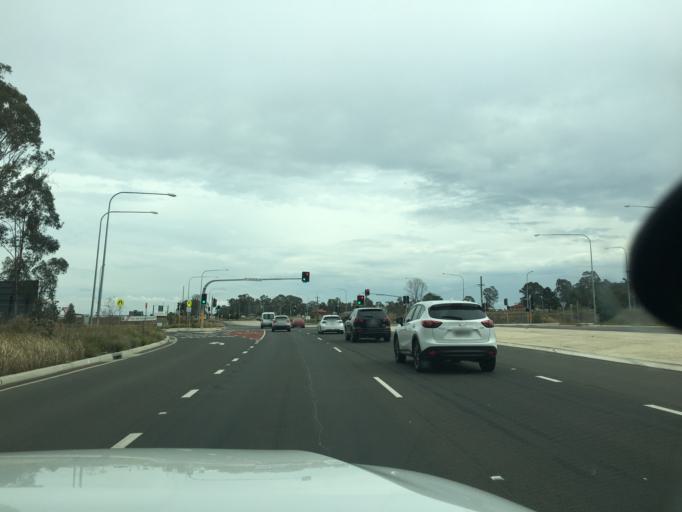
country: AU
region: New South Wales
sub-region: Campbelltown Municipality
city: Denham Court
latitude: -33.9815
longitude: 150.8003
